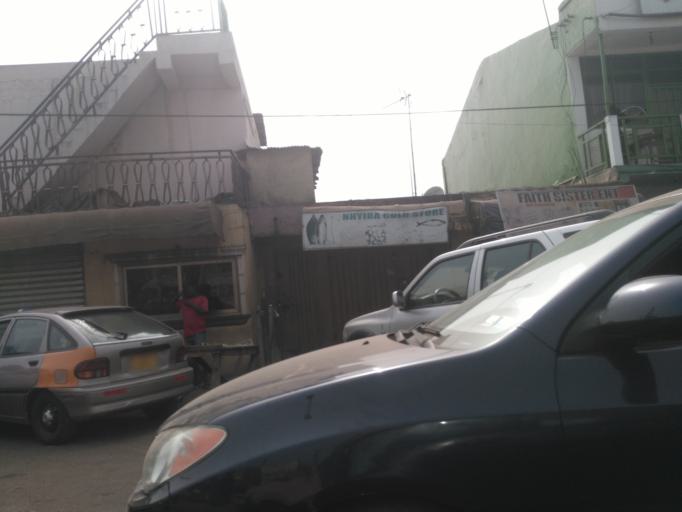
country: GH
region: Ashanti
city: Kumasi
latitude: 6.6868
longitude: -1.6154
